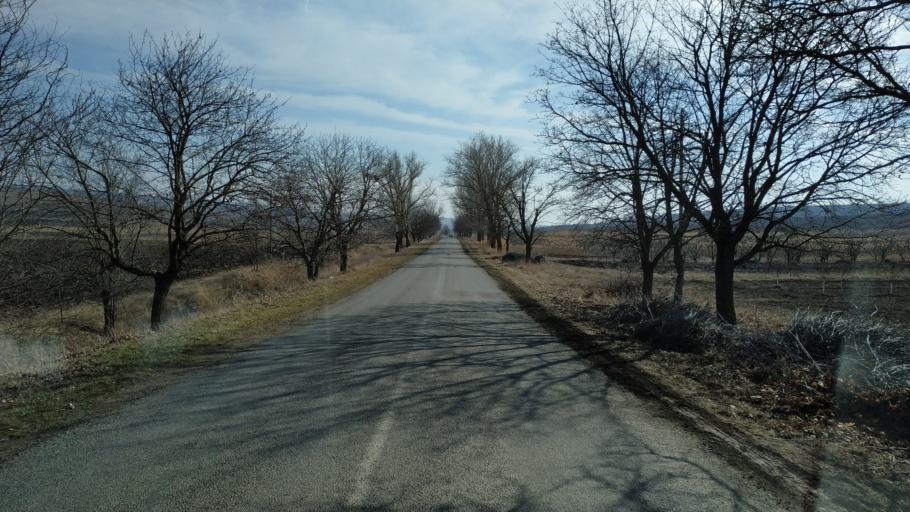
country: MD
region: Nisporeni
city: Nisporeni
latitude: 47.0983
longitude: 28.1307
